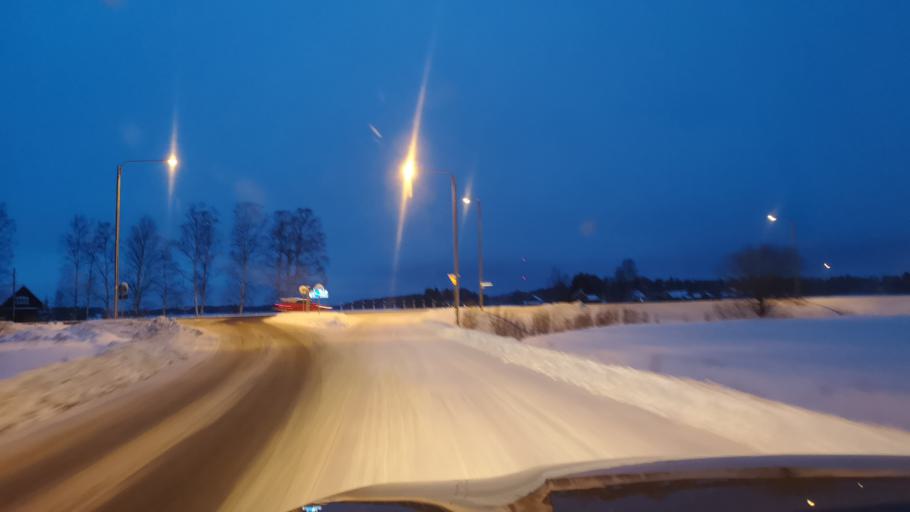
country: FI
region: Varsinais-Suomi
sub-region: Loimaa
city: Loimaa
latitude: 60.8843
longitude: 23.0891
